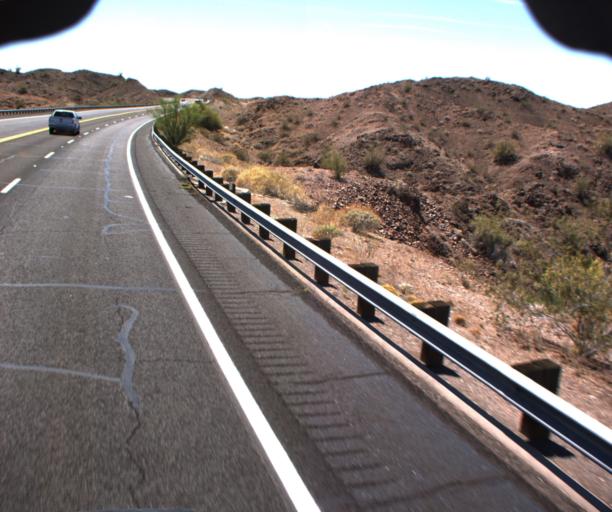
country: US
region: Arizona
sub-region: La Paz County
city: Cienega Springs
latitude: 34.2031
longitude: -114.2075
